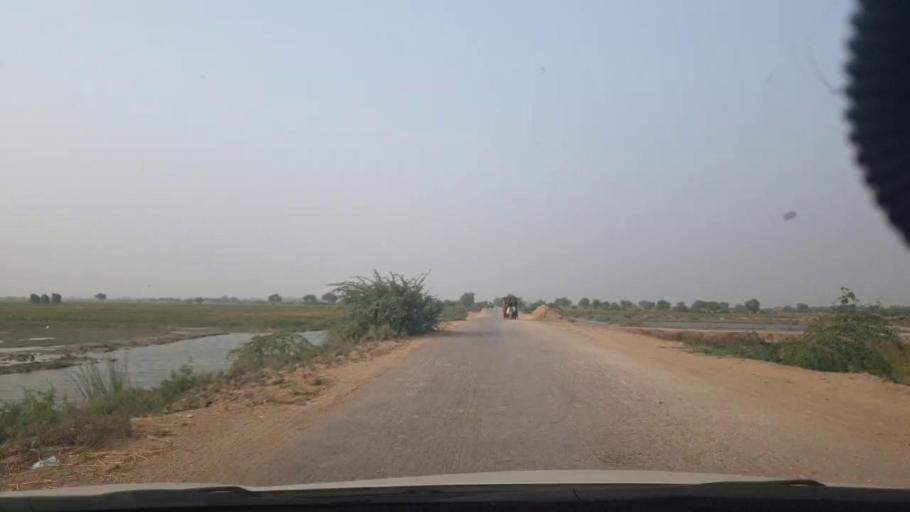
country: PK
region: Sindh
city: Bulri
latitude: 24.7789
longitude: 68.4198
